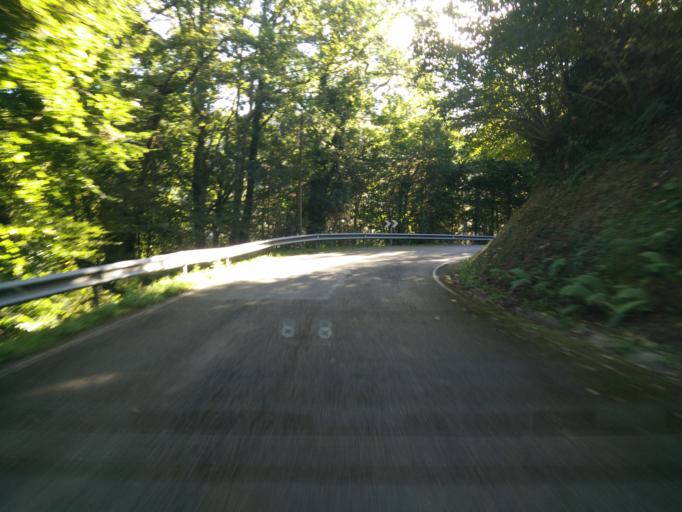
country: ES
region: Cantabria
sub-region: Provincia de Cantabria
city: San Pedro del Romeral
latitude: 43.1291
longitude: -3.8138
